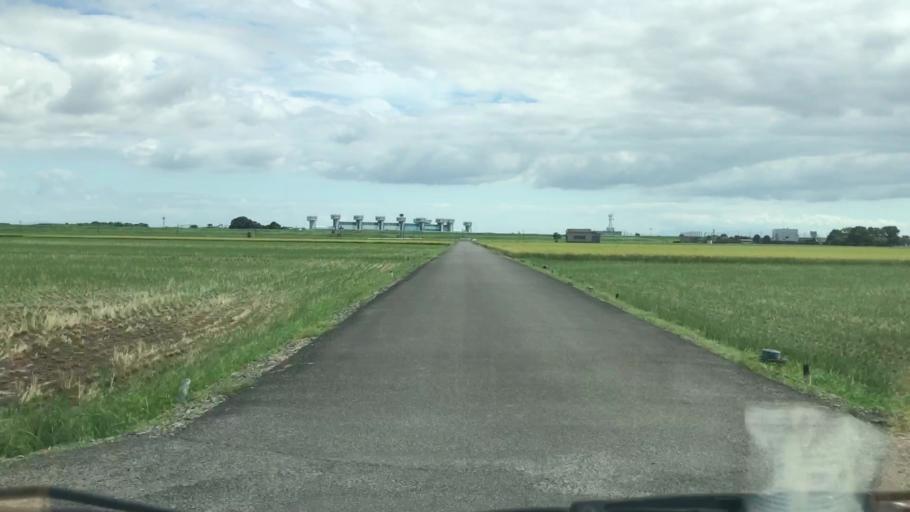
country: JP
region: Saga Prefecture
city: Saga-shi
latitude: 33.2114
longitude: 130.1845
